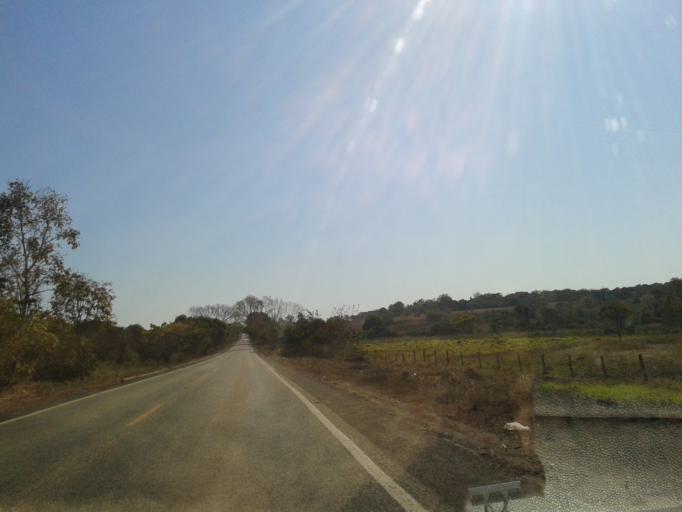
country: BR
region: Goias
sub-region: Mozarlandia
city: Mozarlandia
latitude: -14.5766
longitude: -50.5029
